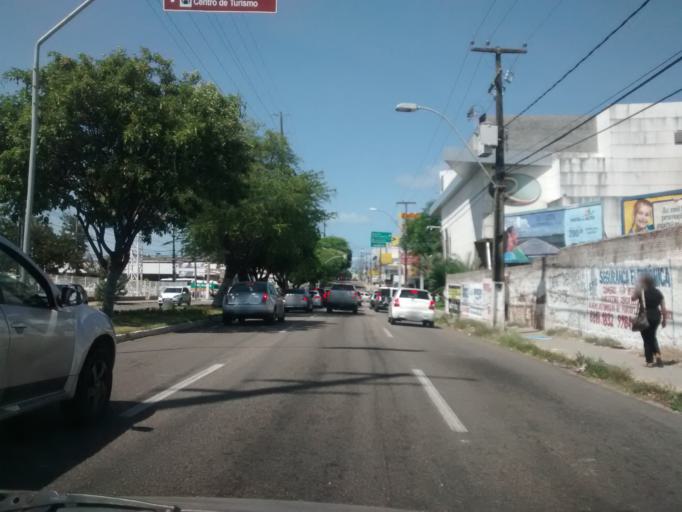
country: BR
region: Rio Grande do Norte
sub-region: Natal
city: Natal
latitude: -5.8145
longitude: -35.2110
